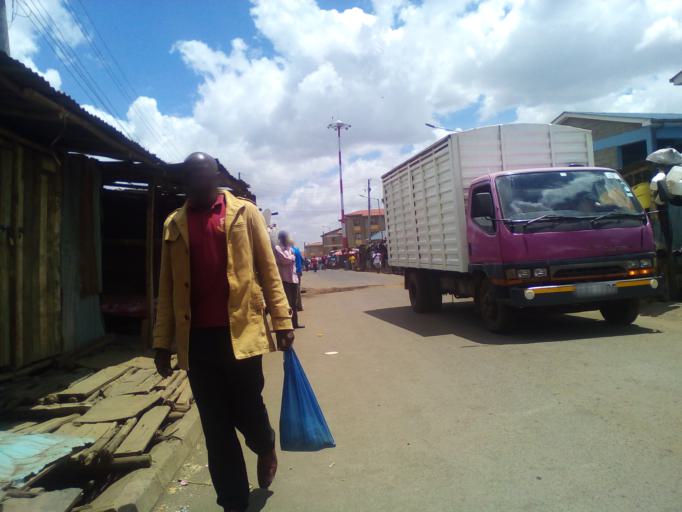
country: KE
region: Nairobi Area
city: Nairobi
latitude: -1.3153
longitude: 36.8039
